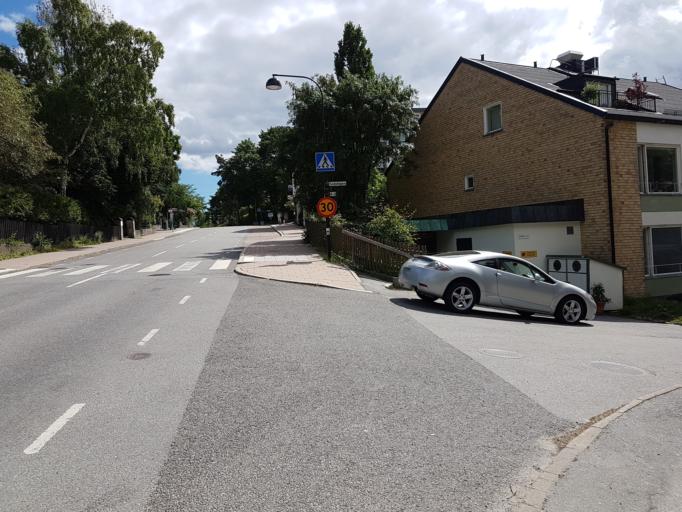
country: SE
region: Stockholm
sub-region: Lidingo
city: Lidingoe
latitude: 59.3607
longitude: 18.1203
